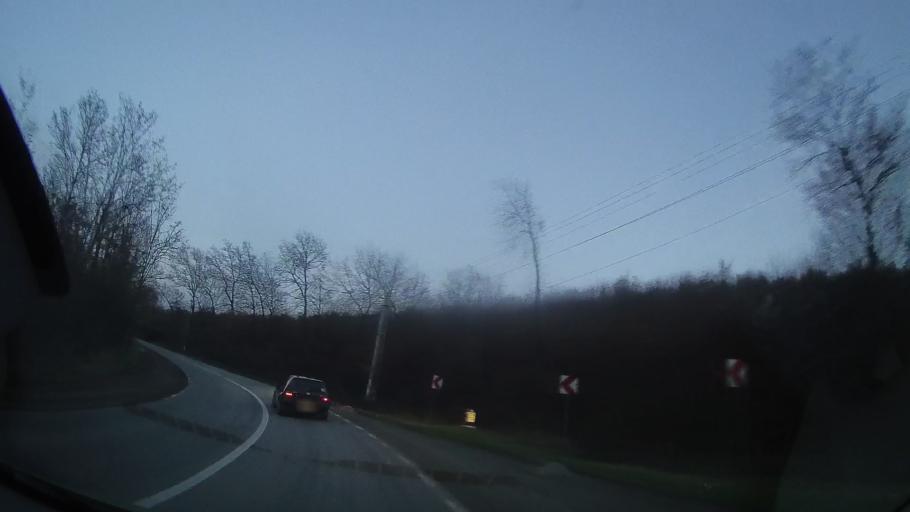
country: RO
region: Cluj
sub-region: Comuna Mociu
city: Mociu
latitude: 46.7919
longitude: 24.0588
